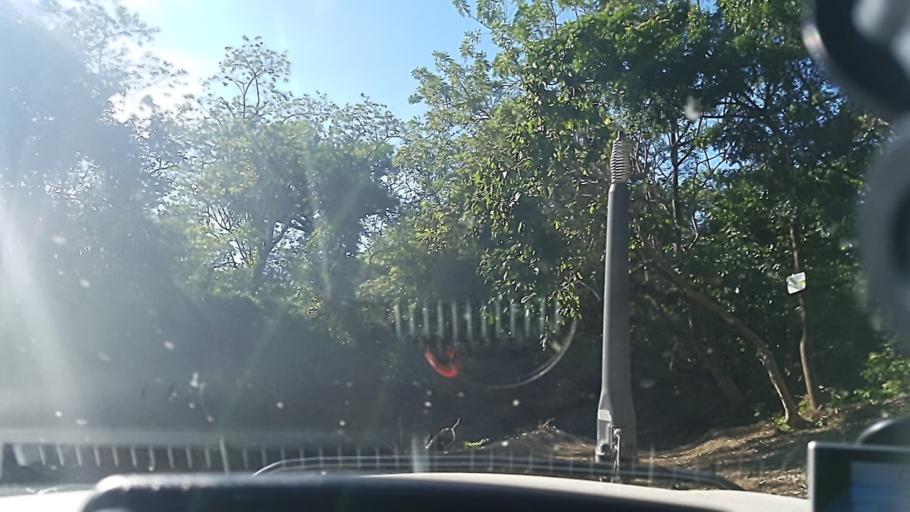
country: NI
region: Rivas
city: Tola
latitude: 11.5415
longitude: -86.1187
